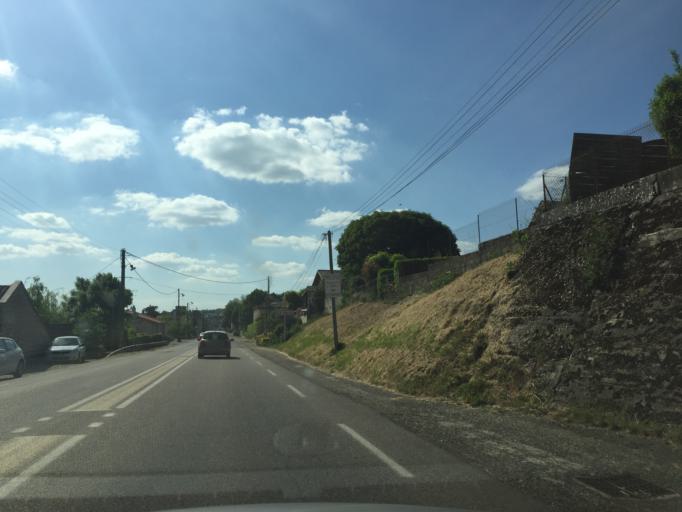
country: FR
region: Aquitaine
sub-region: Departement de la Gironde
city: La Reole
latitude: 44.5802
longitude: -0.0257
